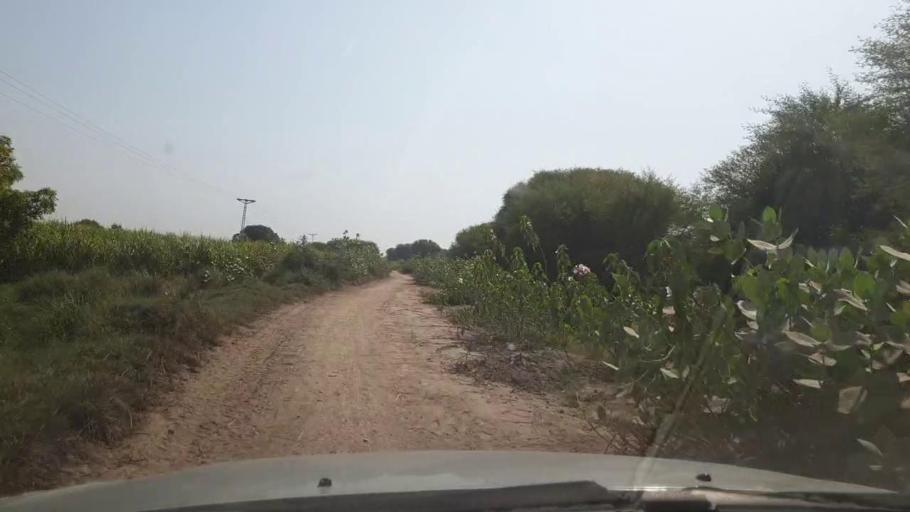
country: PK
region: Sindh
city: Bulri
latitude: 24.8669
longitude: 68.3108
